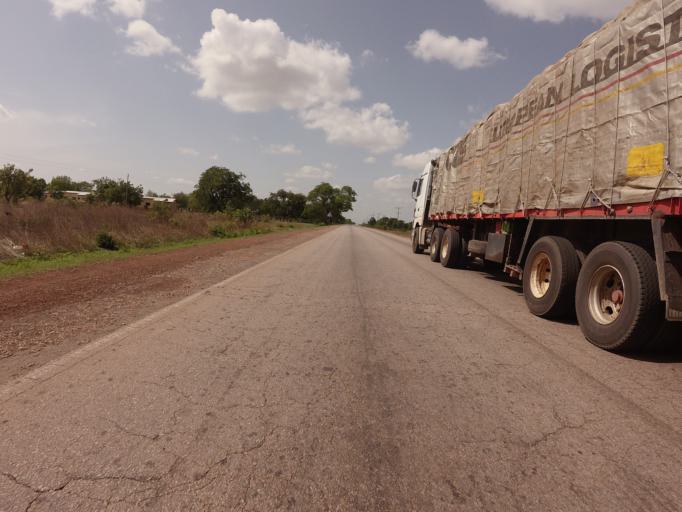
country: GH
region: Northern
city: Savelugu
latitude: 9.8779
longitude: -0.8713
